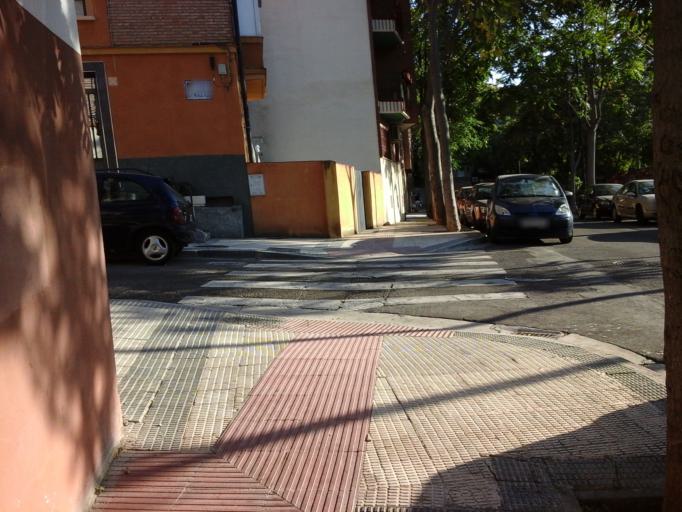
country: ES
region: Aragon
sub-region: Provincia de Zaragoza
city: Zaragoza
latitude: 41.6326
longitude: -0.8736
